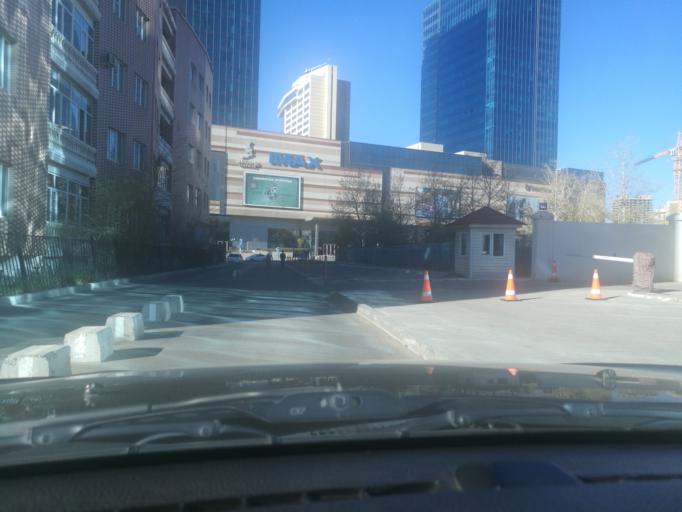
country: MN
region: Ulaanbaatar
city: Ulaanbaatar
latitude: 47.9133
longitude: 106.9239
